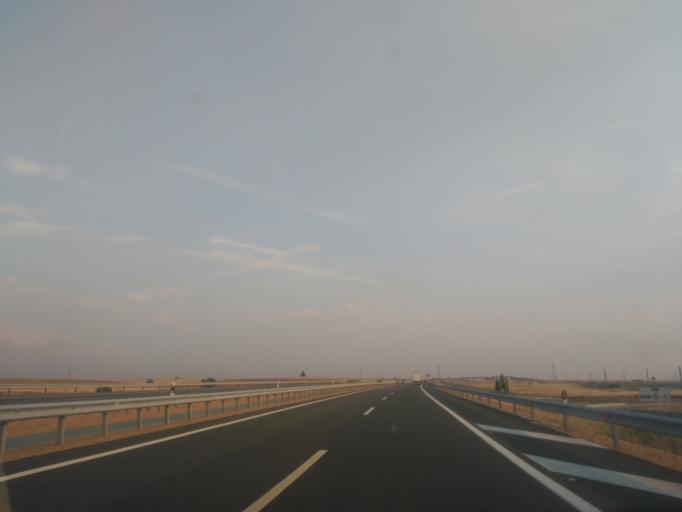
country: ES
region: Castille and Leon
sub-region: Provincia de Zamora
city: Montamarta
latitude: 41.6352
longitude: -5.7902
